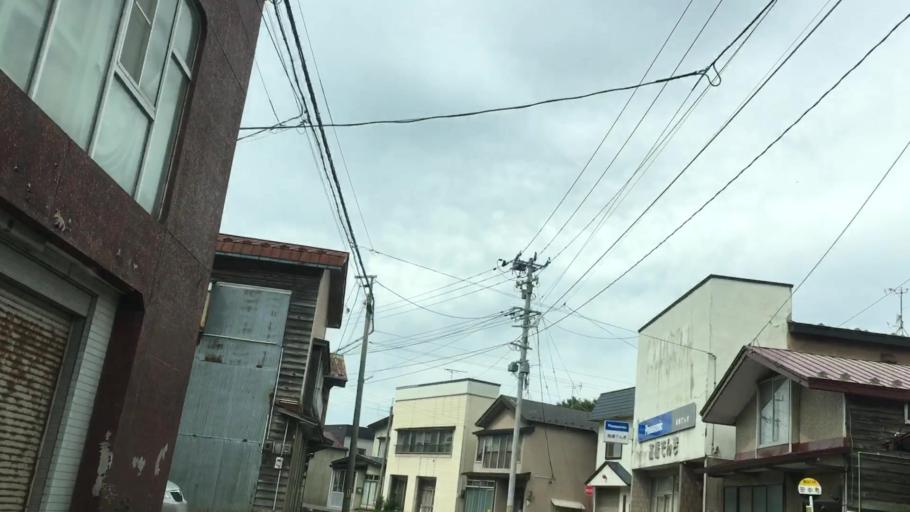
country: JP
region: Aomori
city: Shimokizukuri
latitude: 40.7781
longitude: 140.2169
